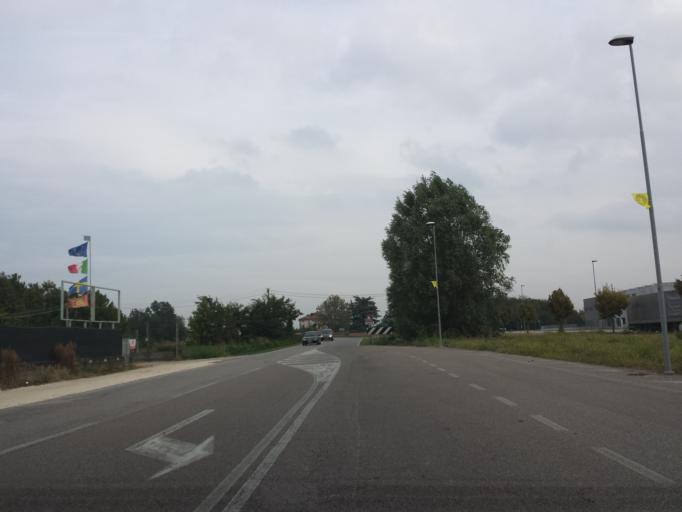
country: IT
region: Veneto
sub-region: Provincia di Verona
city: Albaredo d'Adige
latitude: 45.3298
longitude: 11.2837
